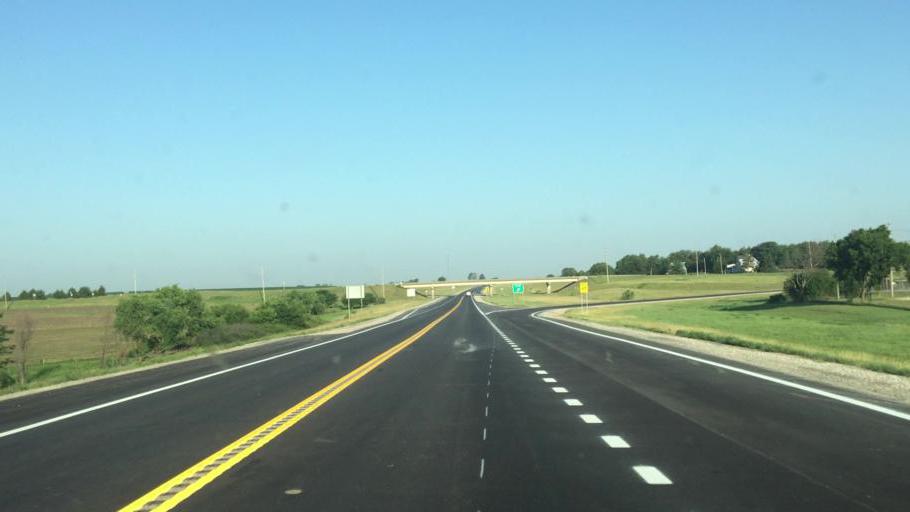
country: US
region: Kansas
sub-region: Brown County
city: Hiawatha
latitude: 39.8408
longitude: -95.5408
